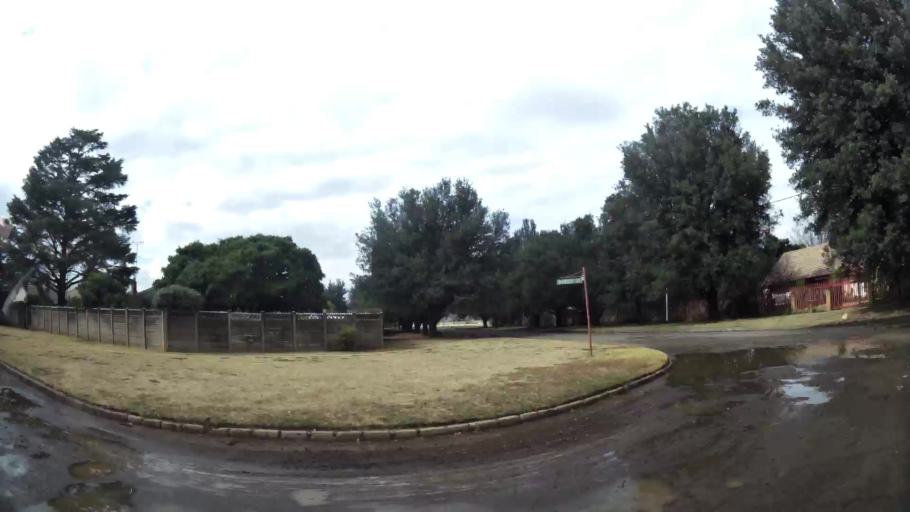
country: ZA
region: Gauteng
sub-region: Sedibeng District Municipality
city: Vereeniging
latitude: -26.6507
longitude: 27.9715
